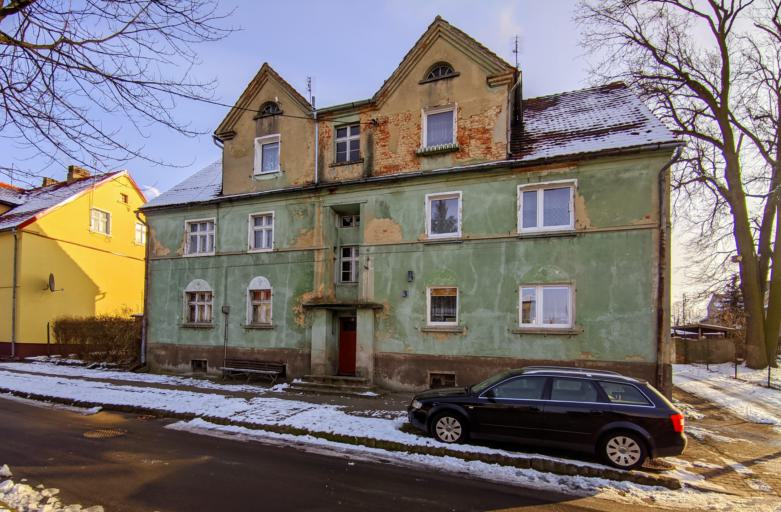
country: PL
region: Lubusz
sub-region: Powiat nowosolski
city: Nowe Miasteczko
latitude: 51.6885
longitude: 15.7335
